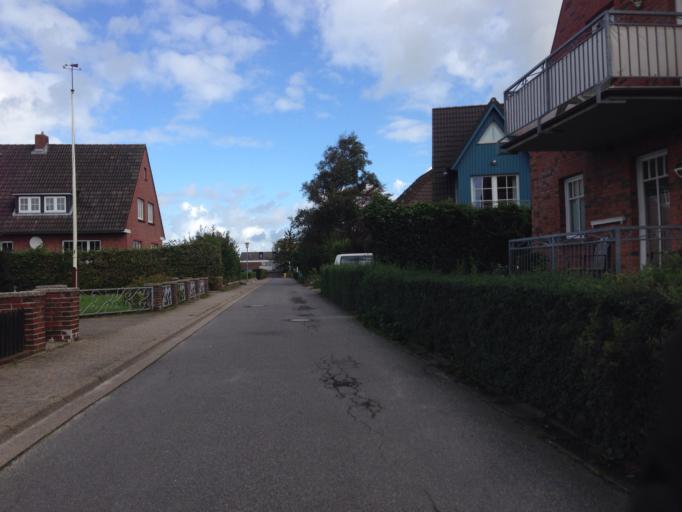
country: DE
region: Schleswig-Holstein
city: Wyk auf Fohr
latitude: 54.6895
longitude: 8.5645
